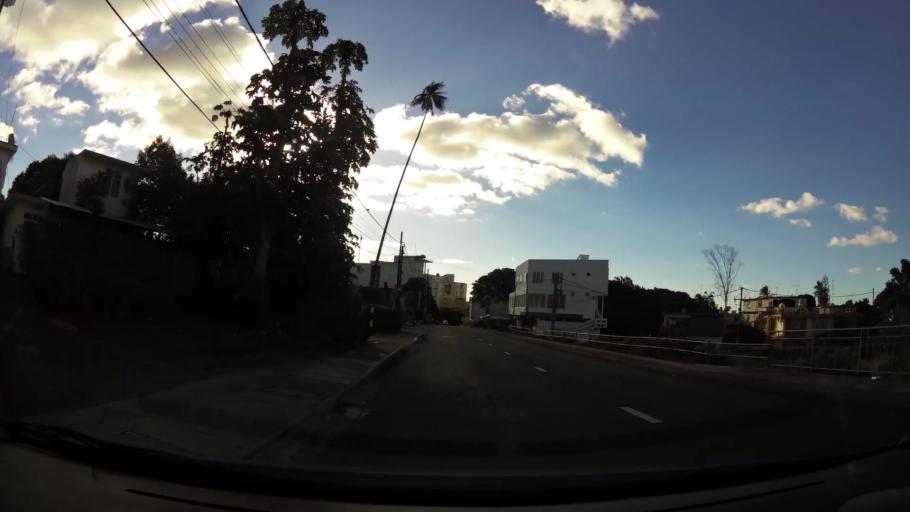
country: MU
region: Plaines Wilhems
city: Ebene
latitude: -20.2323
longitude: 57.4689
